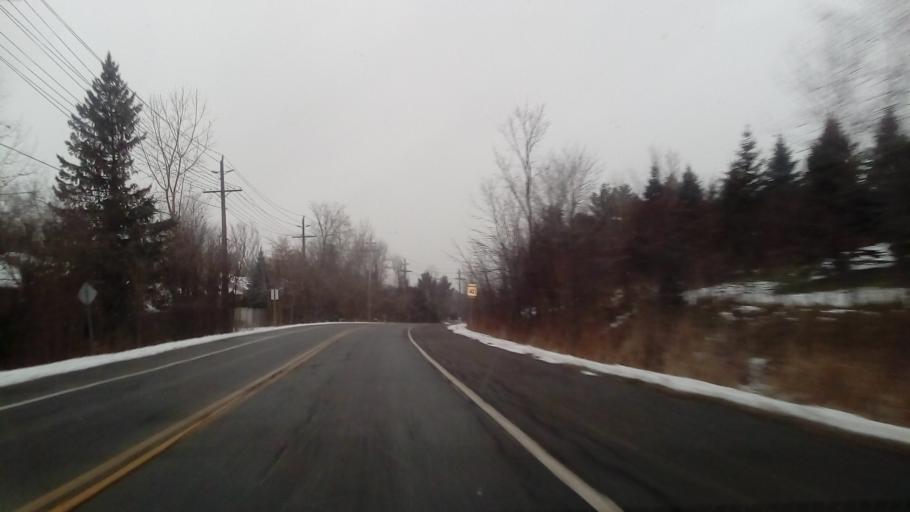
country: CA
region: Ontario
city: Ottawa
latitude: 45.4408
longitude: -75.5726
